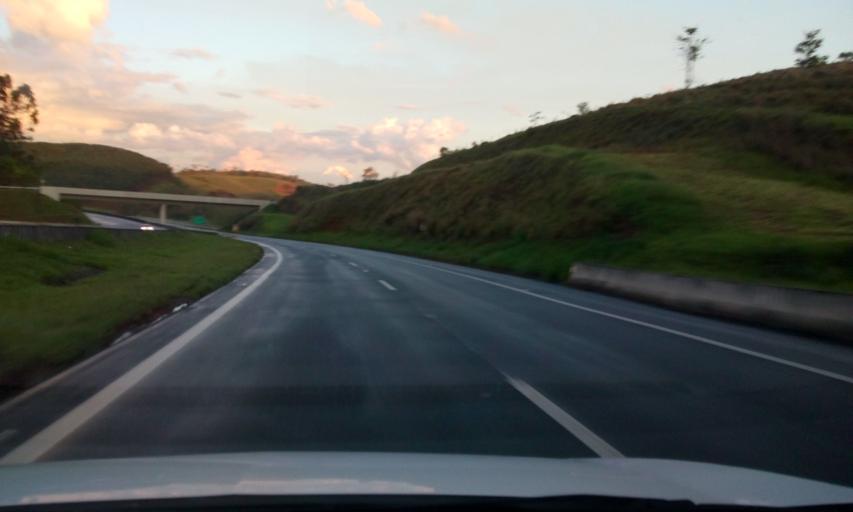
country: BR
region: Sao Paulo
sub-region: Santa Isabel
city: Santa Isabel
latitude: -23.2588
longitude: -46.0978
